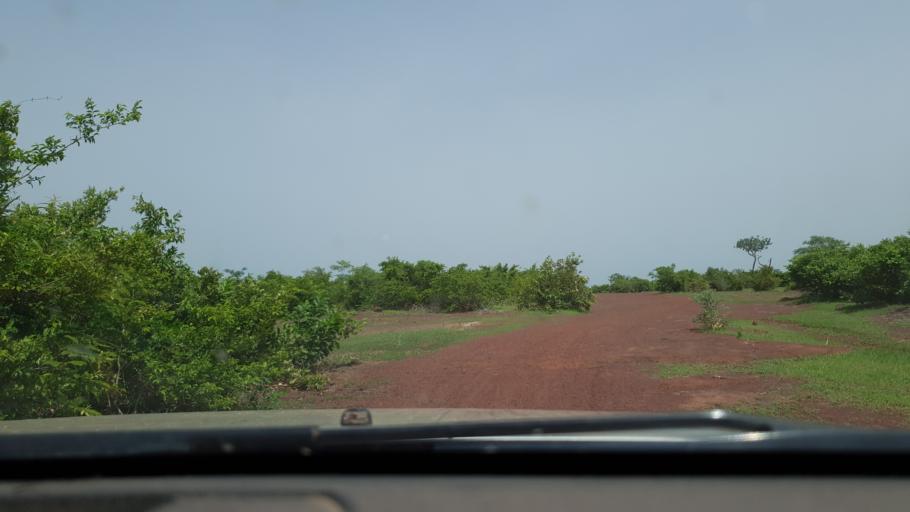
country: ML
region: Koulikoro
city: Koulikoro
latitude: 12.6658
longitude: -7.2294
